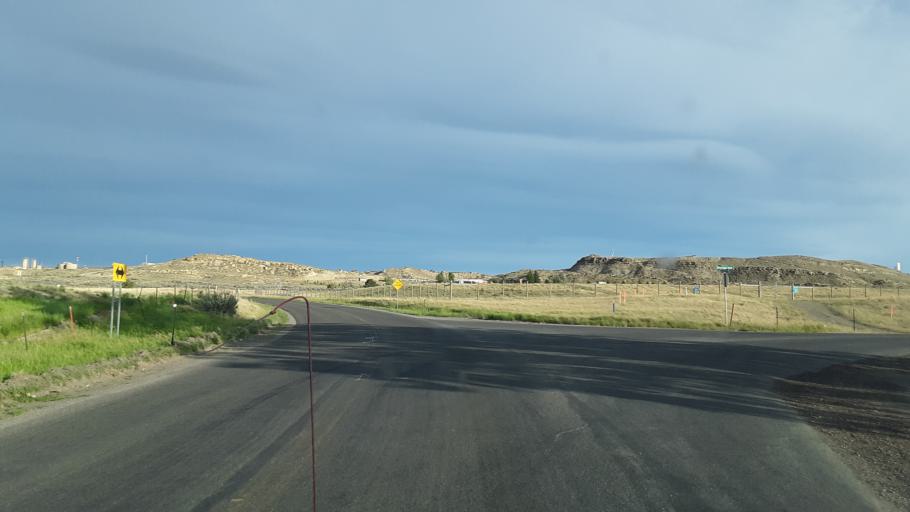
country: US
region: Wyoming
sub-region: Park County
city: Cody
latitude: 44.5302
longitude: -109.0107
